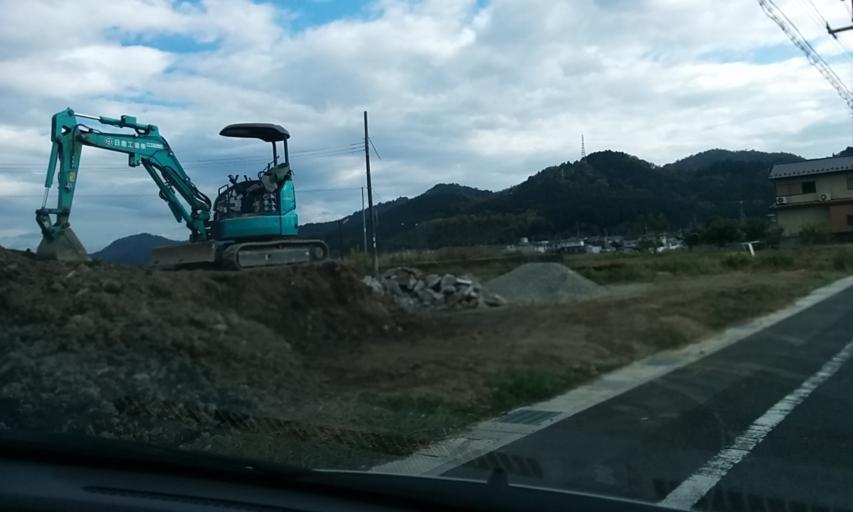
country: JP
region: Kyoto
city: Fukuchiyama
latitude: 35.3047
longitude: 135.1768
